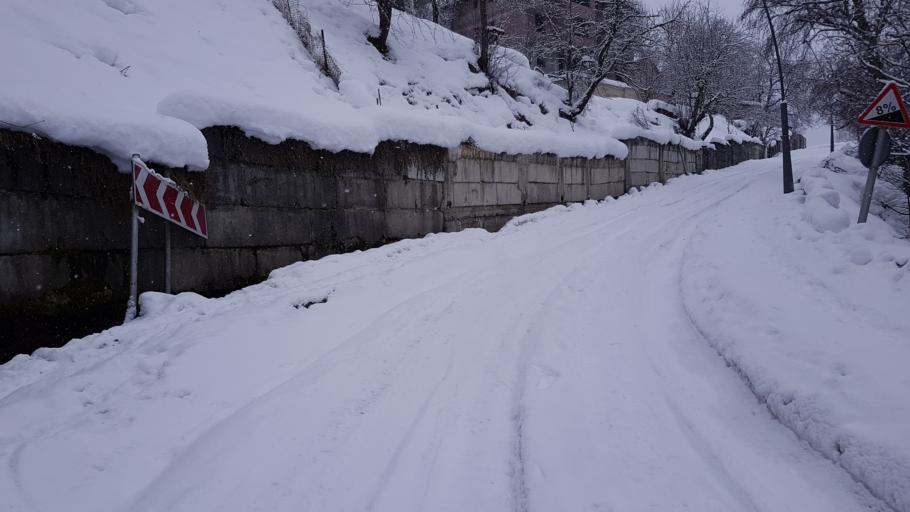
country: GE
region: Samegrelo and Zemo Svaneti
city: Mest'ia
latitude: 43.0416
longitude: 42.7286
